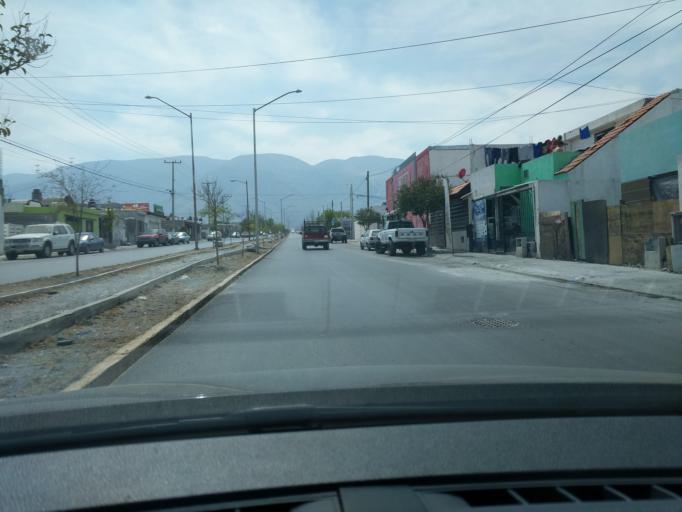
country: MX
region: Coahuila
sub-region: Arteaga
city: Arteaga
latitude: 25.4257
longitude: -100.9028
